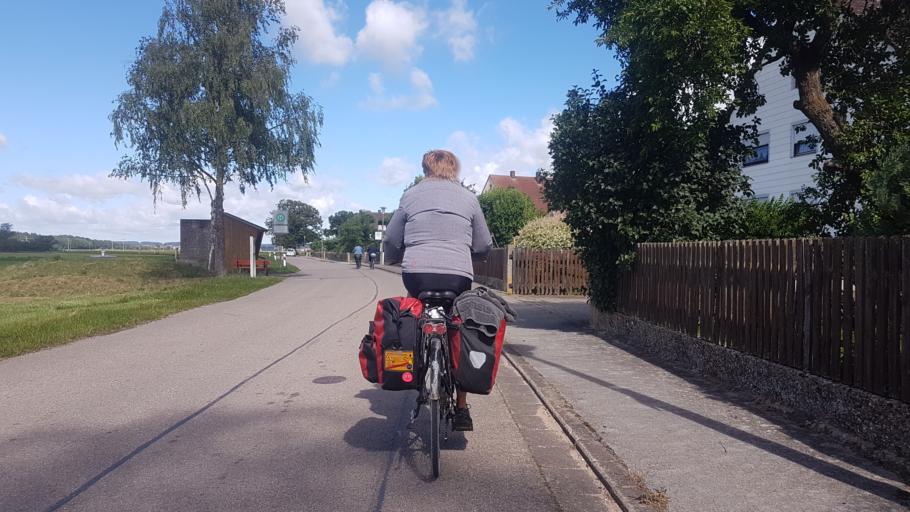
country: DE
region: Bavaria
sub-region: Regierungsbezirk Mittelfranken
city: Weidenbach
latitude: 49.1828
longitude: 10.6211
